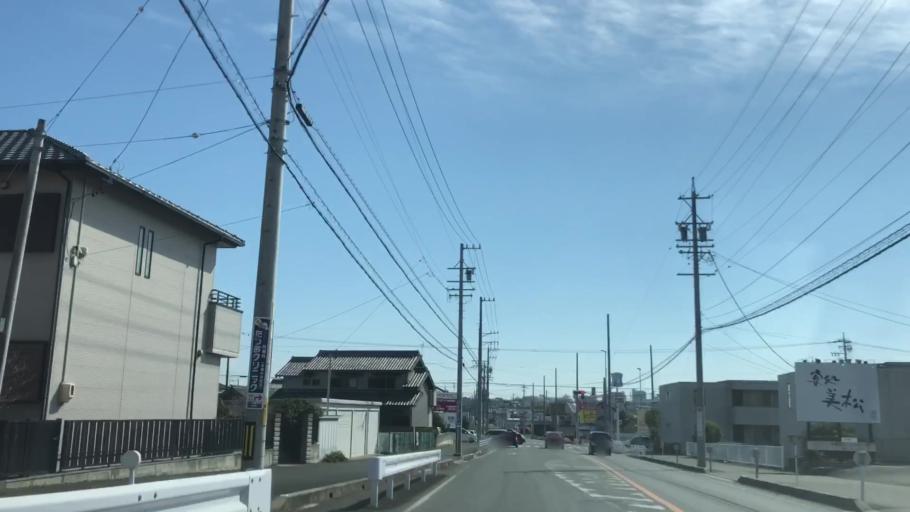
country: JP
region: Aichi
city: Toyohashi
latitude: 34.7197
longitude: 137.4045
